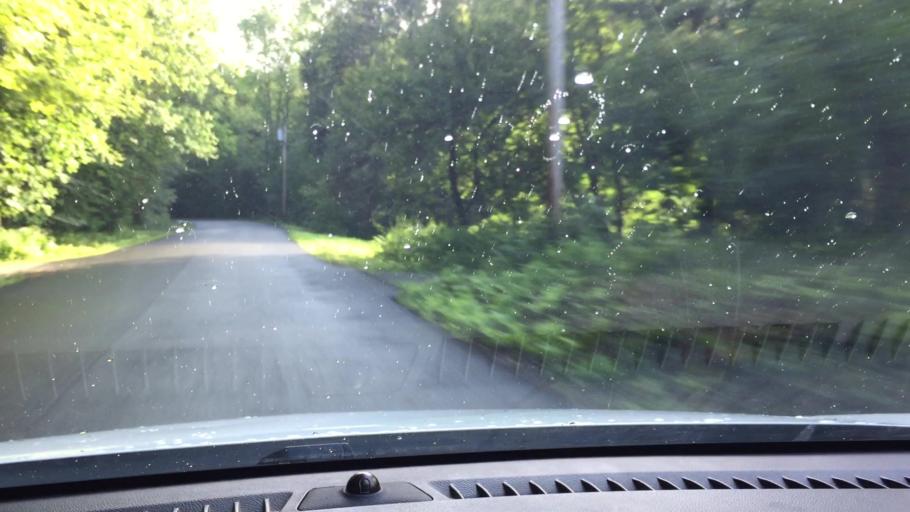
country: US
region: Massachusetts
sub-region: Berkshire County
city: Becket
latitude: 42.3828
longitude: -72.9776
